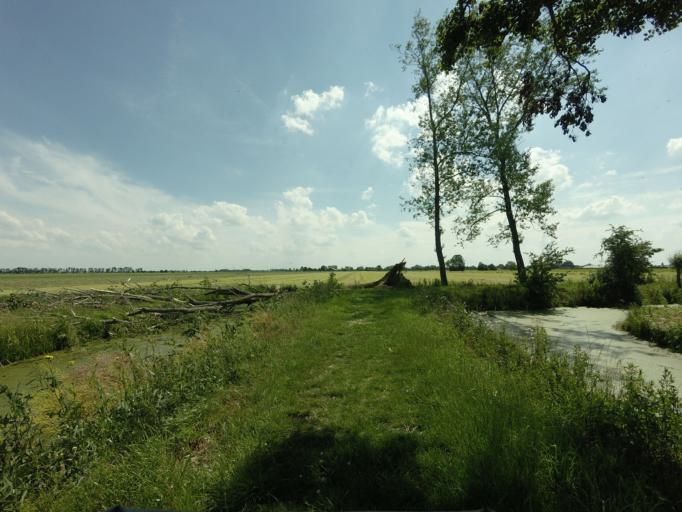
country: NL
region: Utrecht
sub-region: Gemeente Montfoort
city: Montfoort
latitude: 52.0470
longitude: 4.9775
